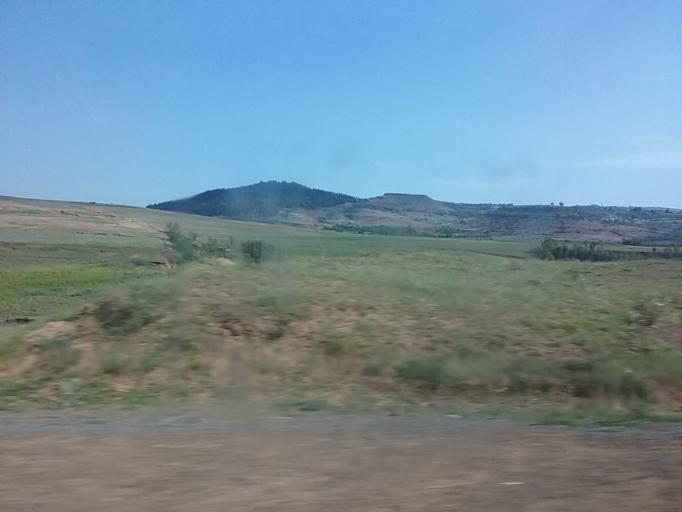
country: LS
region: Berea
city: Teyateyaneng
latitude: -29.0888
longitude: 27.9457
